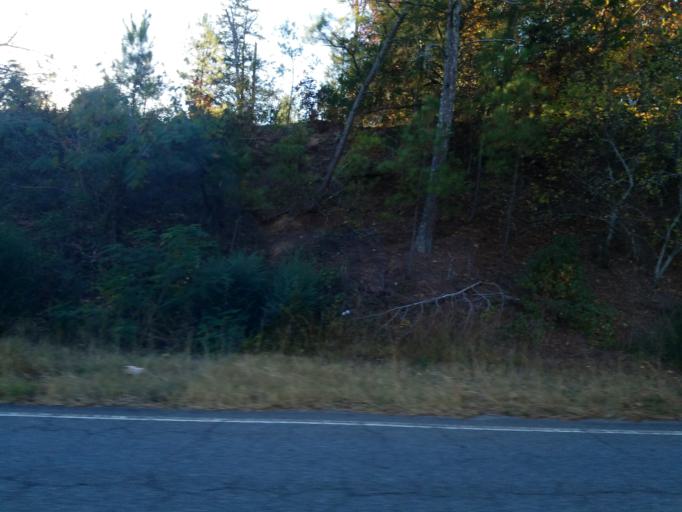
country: US
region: Georgia
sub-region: Bartow County
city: Adairsville
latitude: 34.3548
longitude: -84.9390
